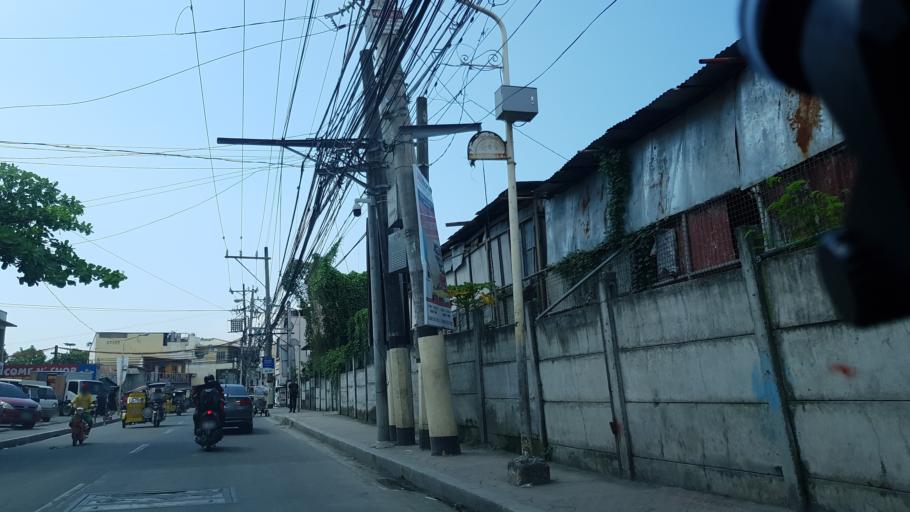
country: PH
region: Calabarzon
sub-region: Province of Rizal
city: Las Pinas
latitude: 14.4706
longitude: 120.9781
